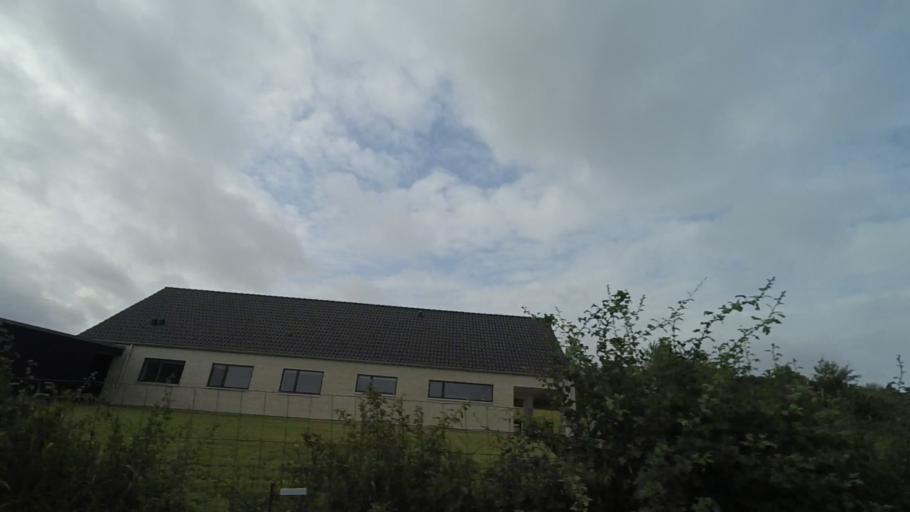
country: DK
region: Central Jutland
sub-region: Syddjurs Kommune
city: Ronde
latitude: 56.3391
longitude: 10.4663
